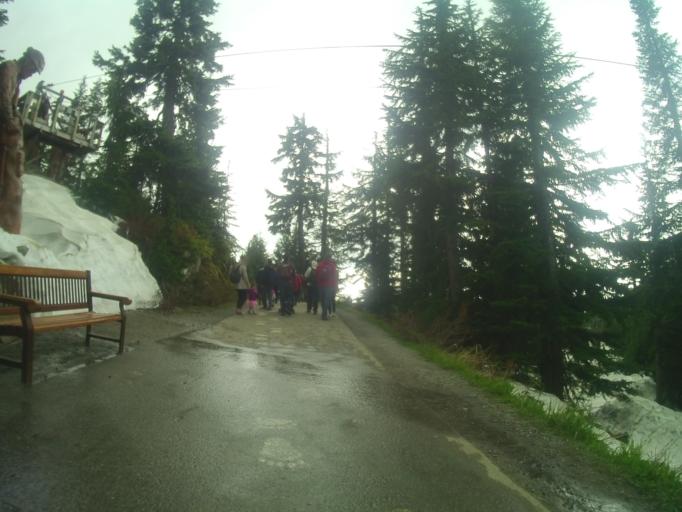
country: CA
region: British Columbia
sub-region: Fraser Valley Regional District
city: North Vancouver
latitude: 49.3803
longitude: -123.0816
